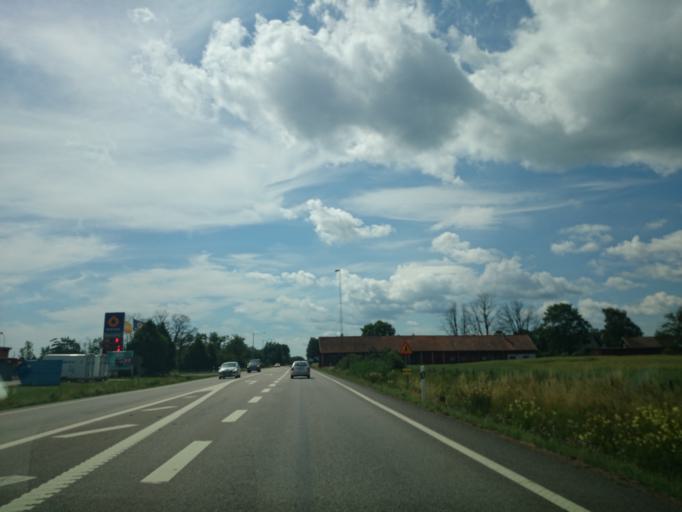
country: SE
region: Kalmar
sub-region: Monsteras Kommun
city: Moensteras
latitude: 57.0361
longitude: 16.4342
